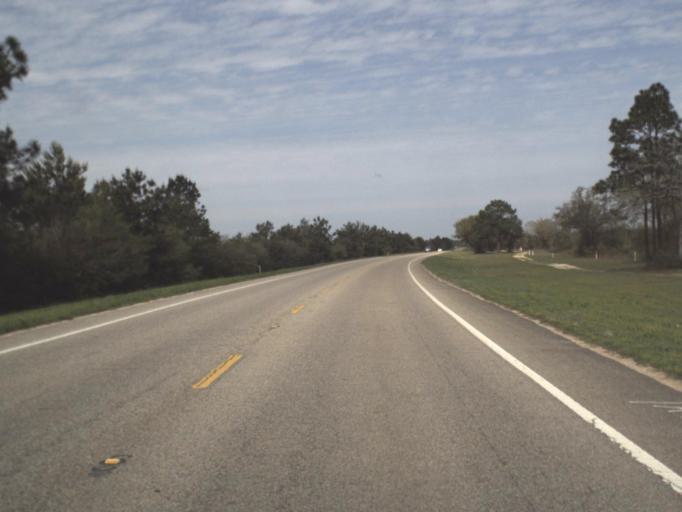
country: US
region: Florida
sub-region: Okaloosa County
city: Crestview
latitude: 30.7448
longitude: -86.4139
